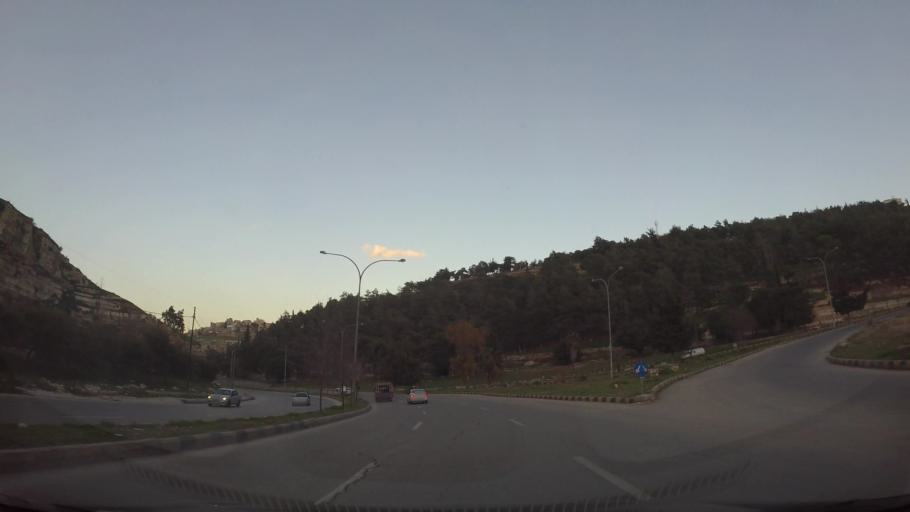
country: JO
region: Amman
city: Al Quwaysimah
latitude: 31.9272
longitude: 35.9182
